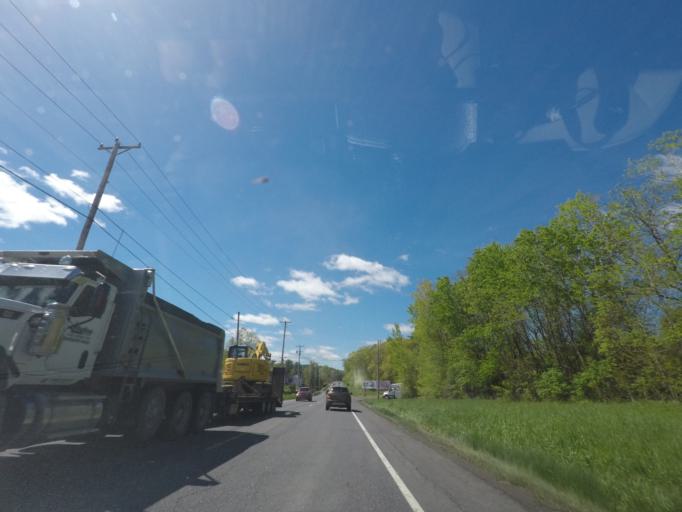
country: US
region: New York
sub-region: Ulster County
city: Lake Katrine
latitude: 42.0052
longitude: -73.9836
